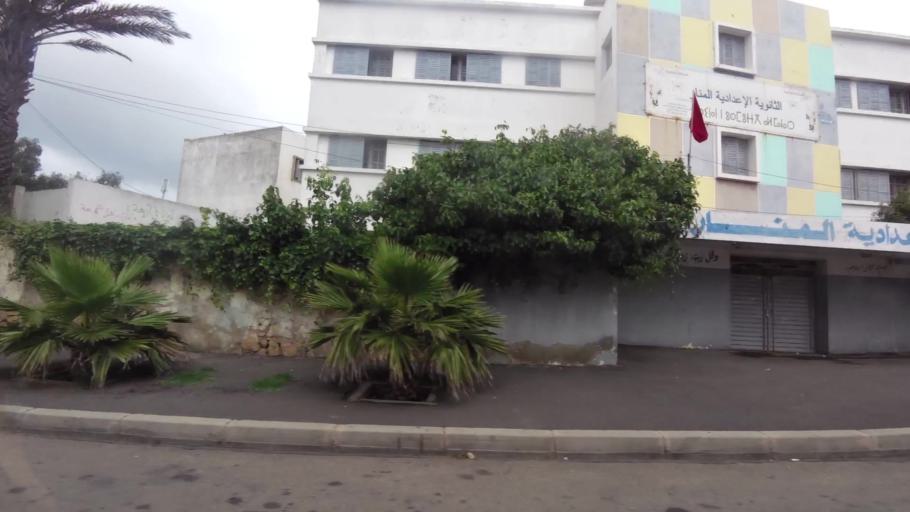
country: MA
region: Grand Casablanca
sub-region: Casablanca
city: Casablanca
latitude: 33.6042
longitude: -7.6559
